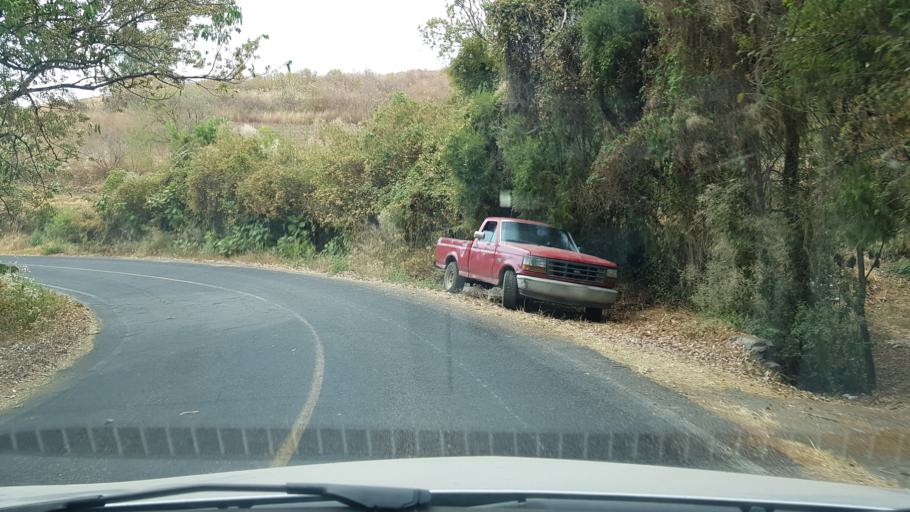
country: MX
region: Morelos
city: Tlacotepec
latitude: 18.8364
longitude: -98.7254
